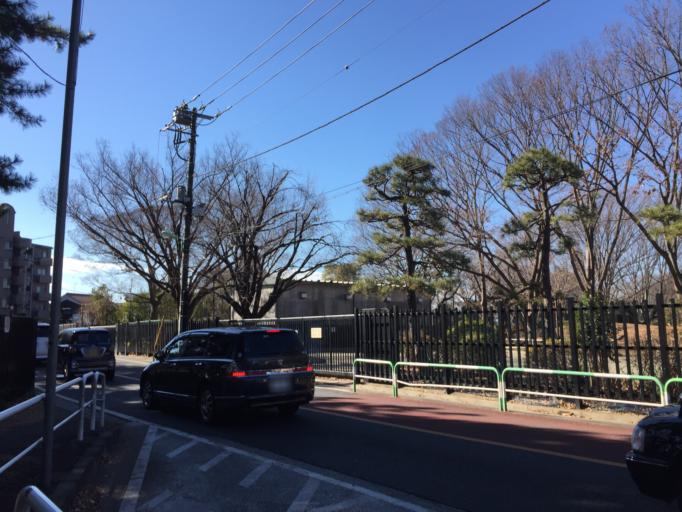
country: JP
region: Tokyo
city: Chofugaoka
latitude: 35.6292
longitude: 139.6147
